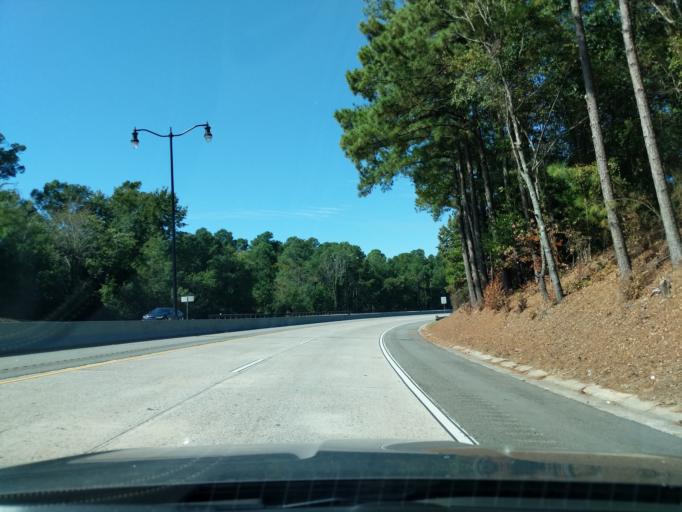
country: US
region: Georgia
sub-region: Richmond County
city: Augusta
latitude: 33.4880
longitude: -82.0086
